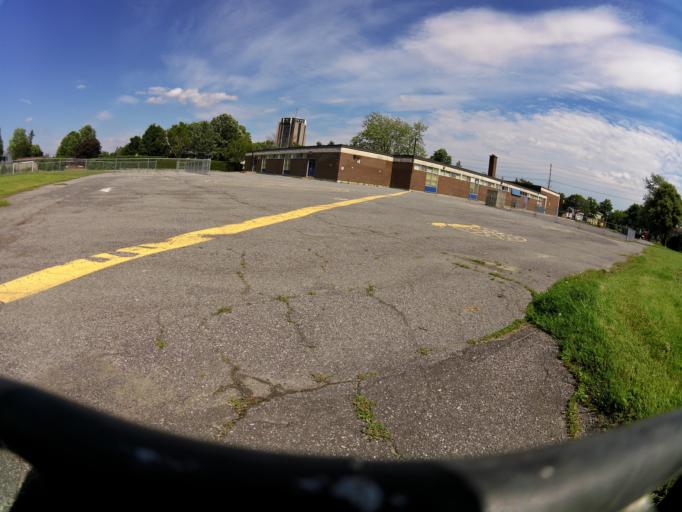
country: CA
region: Ontario
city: Ottawa
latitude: 45.3690
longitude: -75.7101
